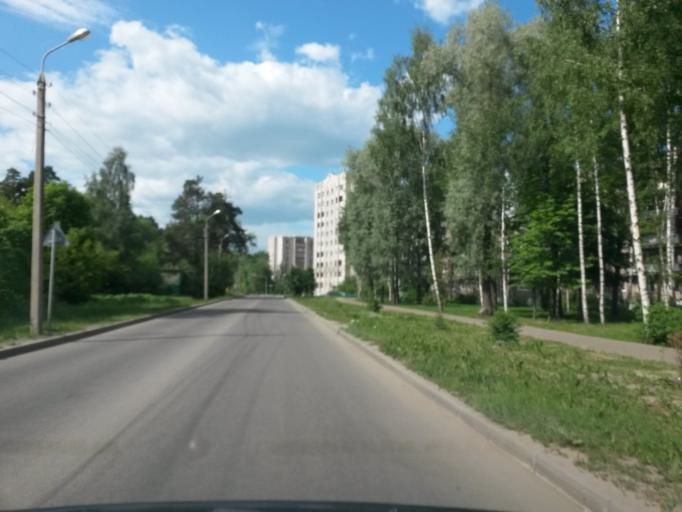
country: RU
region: Jaroslavl
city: Yaroslavl
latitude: 57.6453
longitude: 39.9409
